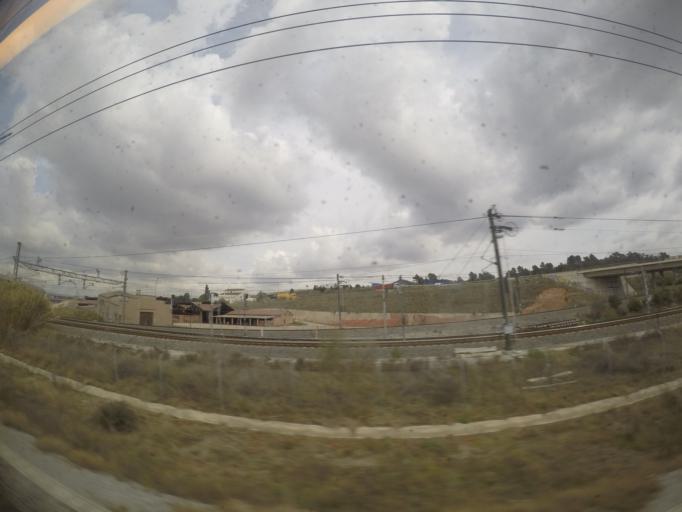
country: ES
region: Catalonia
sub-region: Provincia de Barcelona
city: Palleja
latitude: 41.4387
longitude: 1.9986
